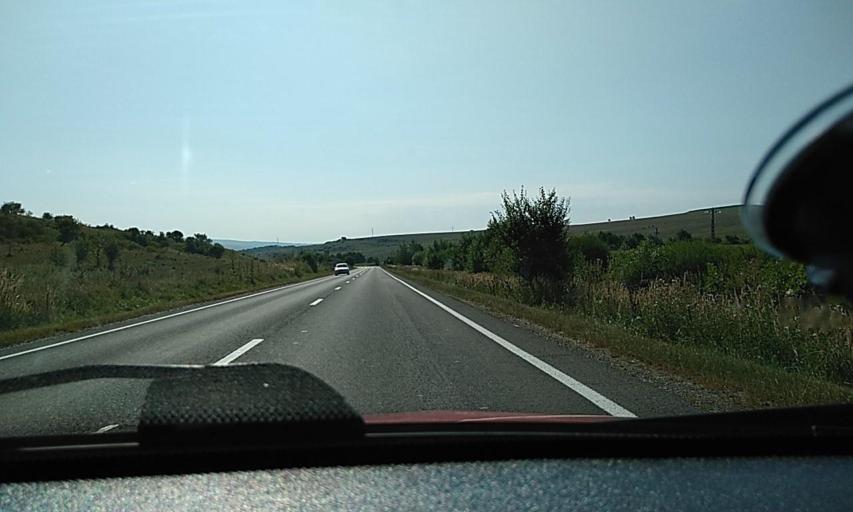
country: RO
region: Brasov
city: Maierus
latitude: 45.9047
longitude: 25.4989
